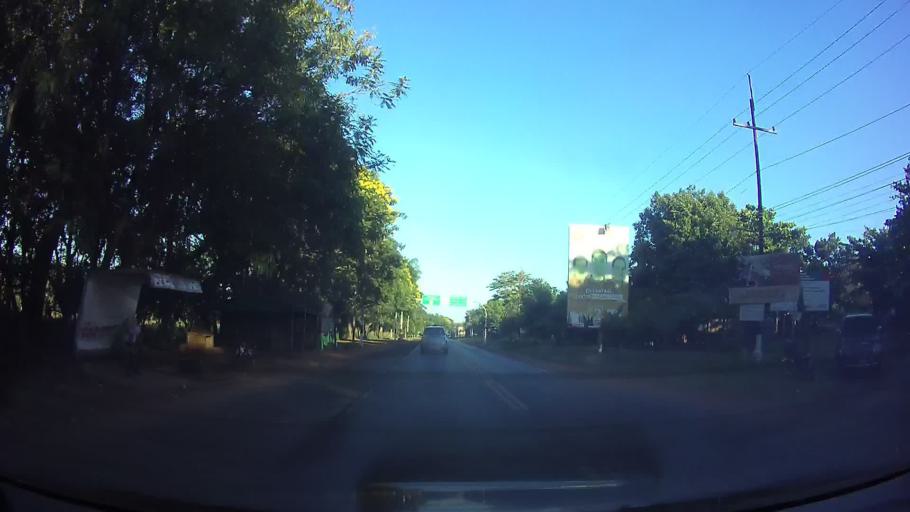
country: PY
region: Central
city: Aregua
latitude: -25.3046
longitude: -57.3981
